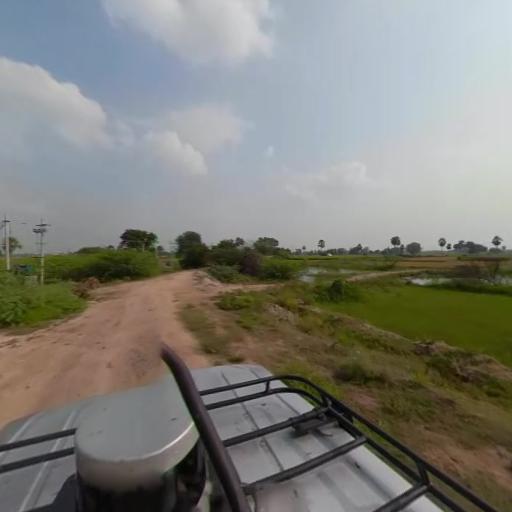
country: IN
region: Telangana
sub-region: Nalgonda
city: Suriapet
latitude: 17.1998
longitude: 79.4893
